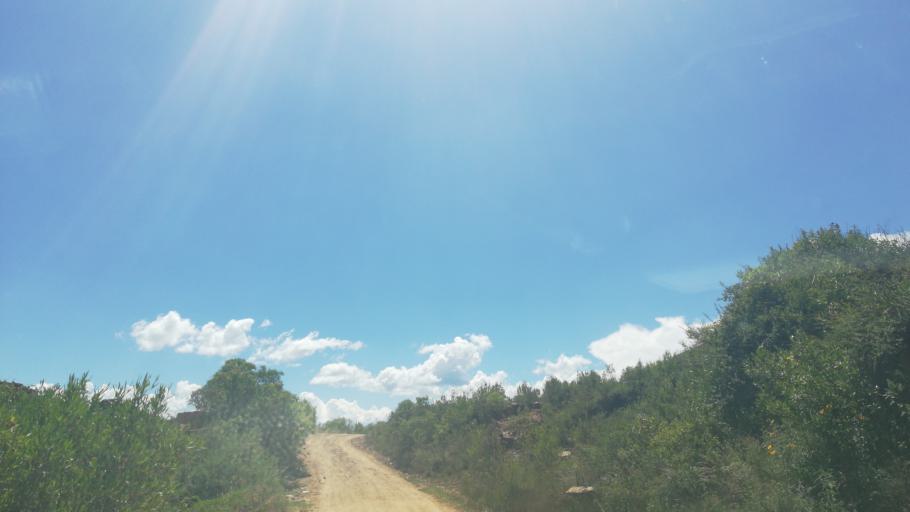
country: BO
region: Cochabamba
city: Totora
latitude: -17.7318
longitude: -65.2280
